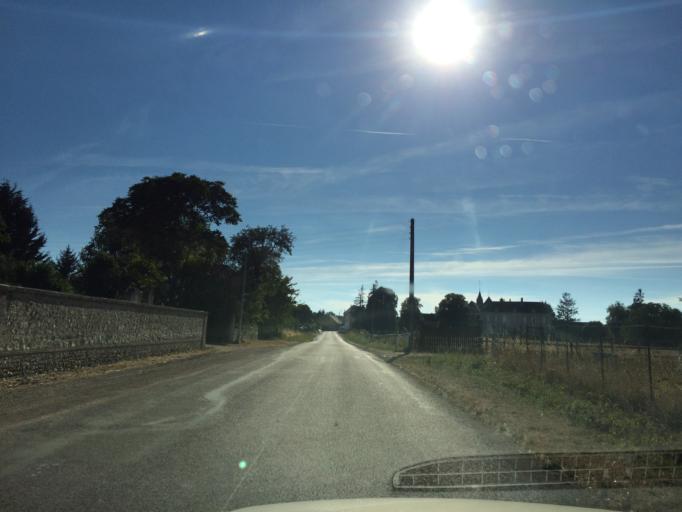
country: FR
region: Bourgogne
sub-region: Departement de l'Yonne
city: Fleury-la-Vallee
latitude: 47.9167
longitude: 3.4439
